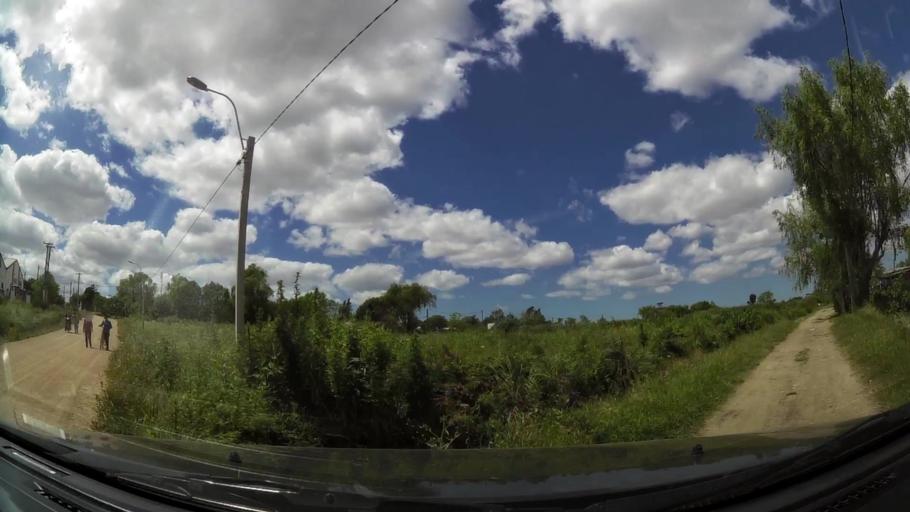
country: UY
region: Canelones
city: Colonia Nicolich
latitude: -34.8163
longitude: -56.0406
